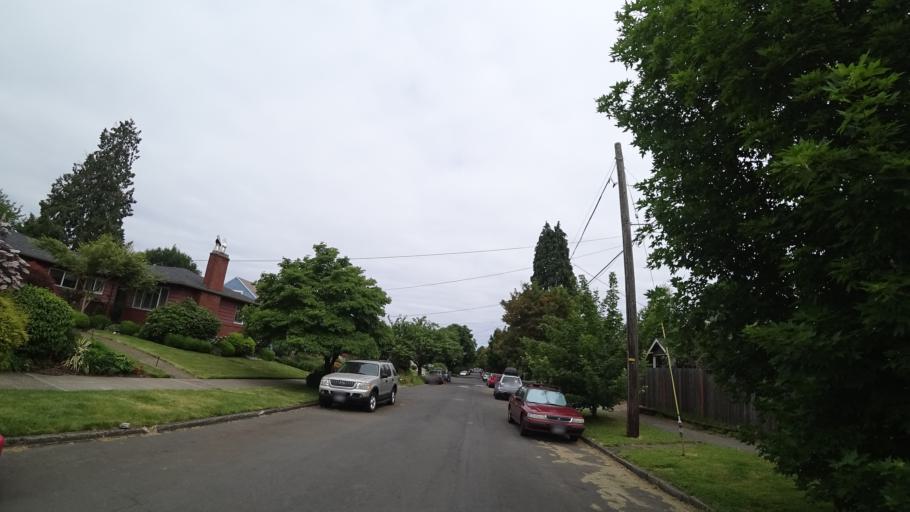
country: US
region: Oregon
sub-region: Multnomah County
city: Portland
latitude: 45.5628
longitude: -122.6328
